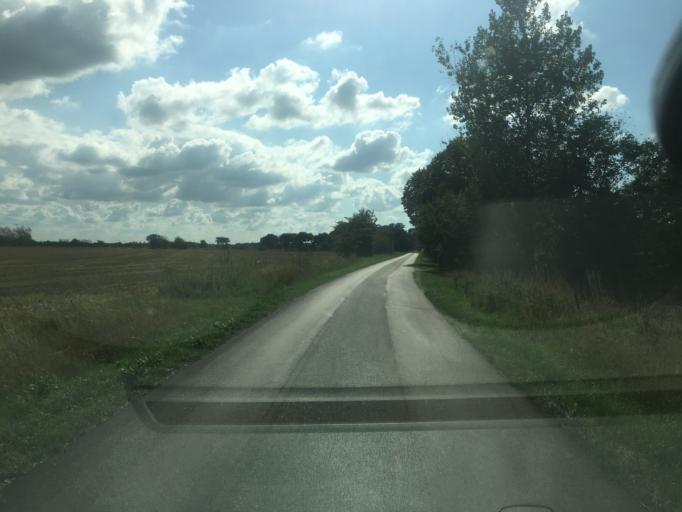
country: DK
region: South Denmark
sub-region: Tonder Kommune
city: Logumkloster
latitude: 54.9840
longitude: 8.9956
